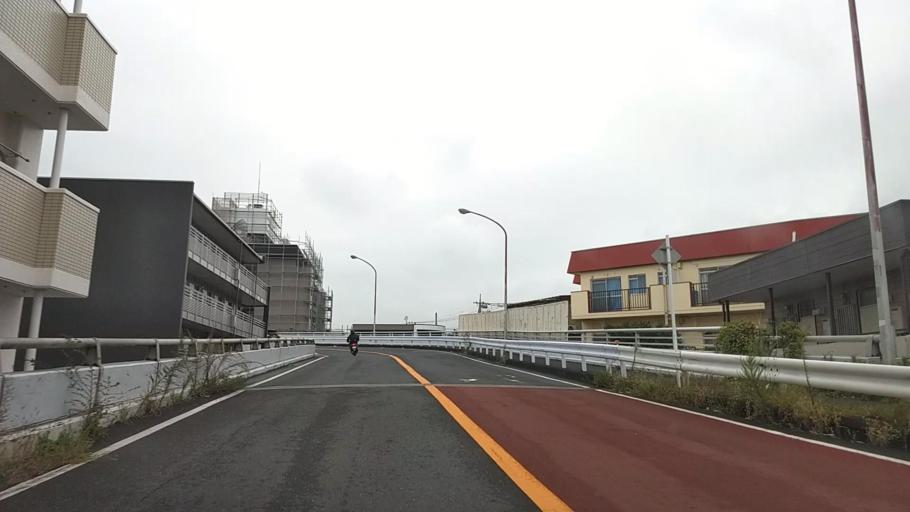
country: JP
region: Kanagawa
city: Fujisawa
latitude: 35.3879
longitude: 139.5346
